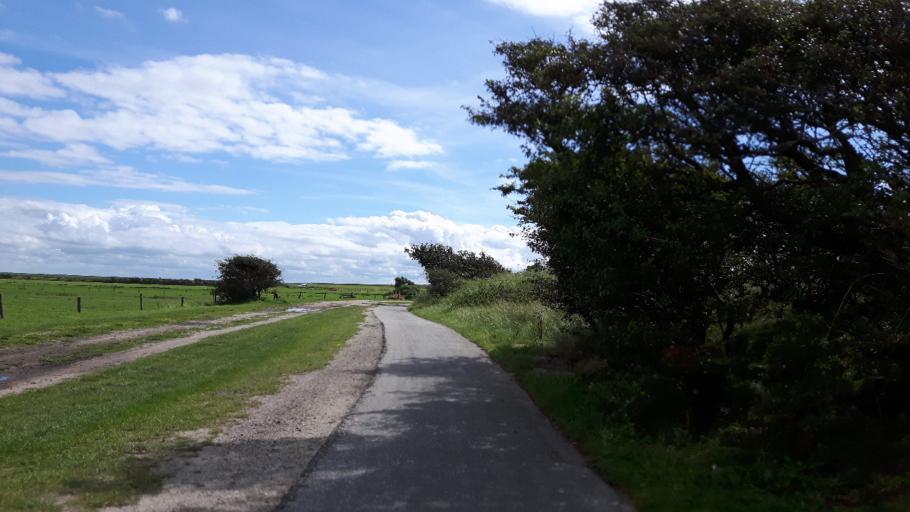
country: NL
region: Friesland
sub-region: Gemeente Ameland
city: Hollum
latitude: 53.4378
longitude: 5.6241
